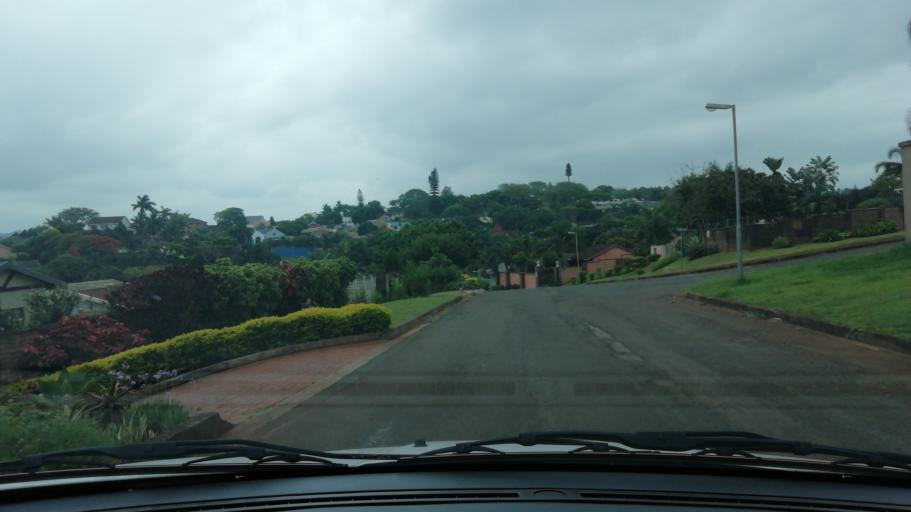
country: ZA
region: KwaZulu-Natal
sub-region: uThungulu District Municipality
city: Empangeni
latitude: -28.7638
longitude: 31.8891
